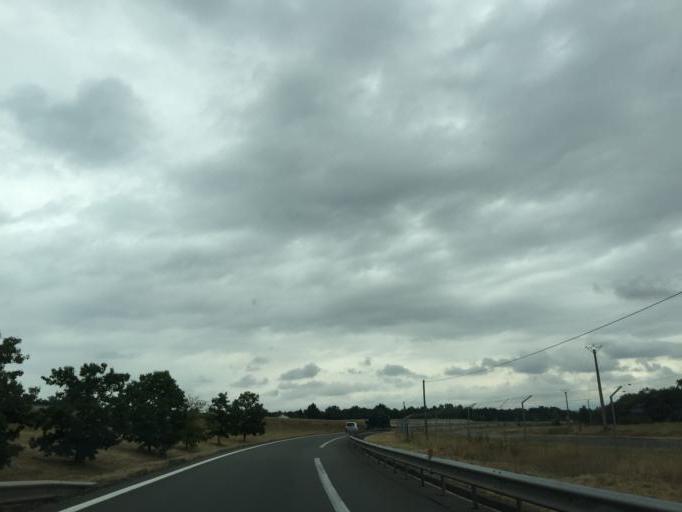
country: FR
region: Rhone-Alpes
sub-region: Departement de la Loire
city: Balbigny
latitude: 45.8191
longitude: 4.1152
